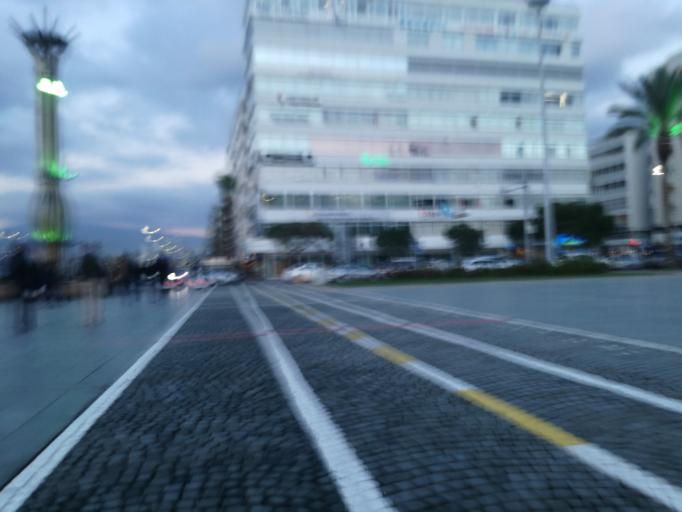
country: TR
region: Izmir
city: Izmir
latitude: 38.4293
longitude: 27.1340
